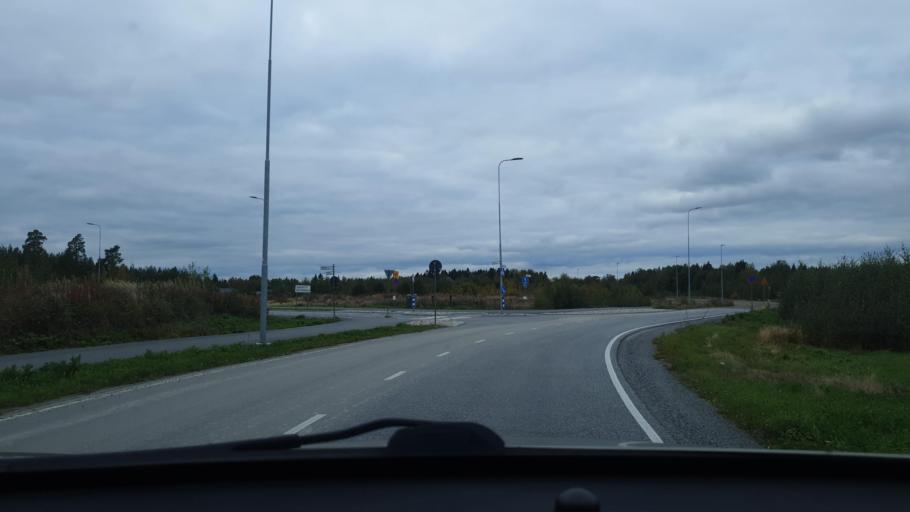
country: FI
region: Ostrobothnia
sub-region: Vaasa
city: Korsholm
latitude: 63.1288
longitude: 21.6604
